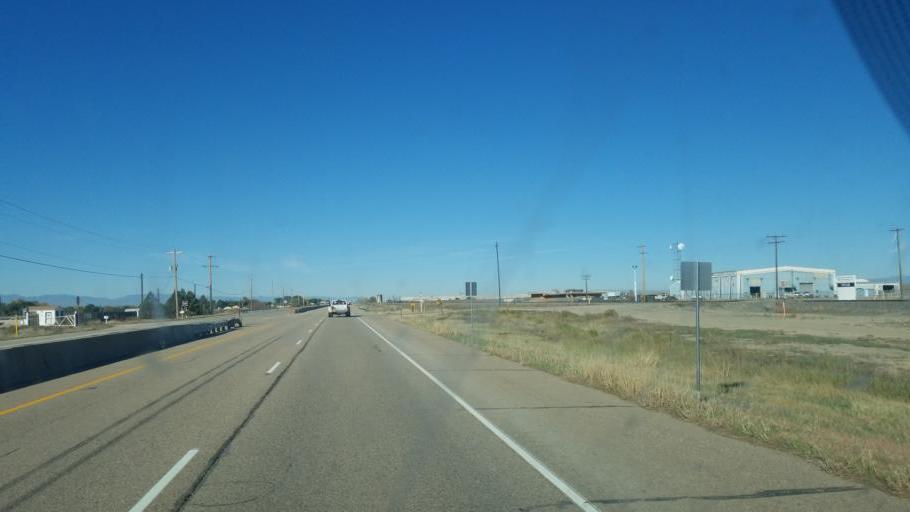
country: US
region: Colorado
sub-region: Pueblo County
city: Pueblo
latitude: 38.2736
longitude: -104.4446
